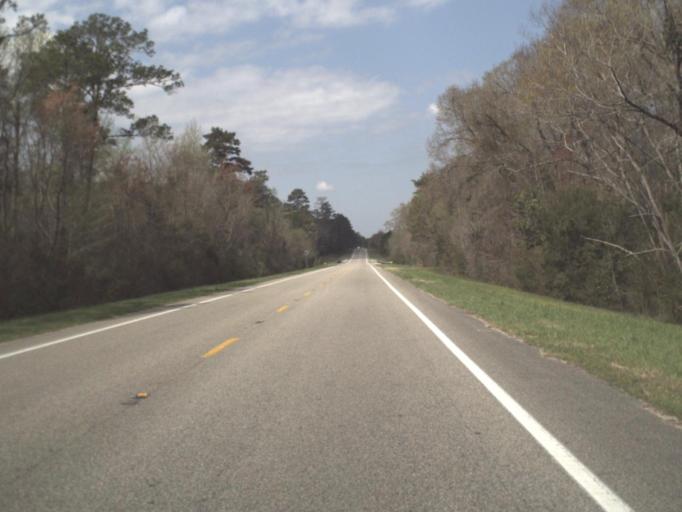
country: US
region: Florida
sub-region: Gadsden County
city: Quincy
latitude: 30.3878
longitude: -84.6673
